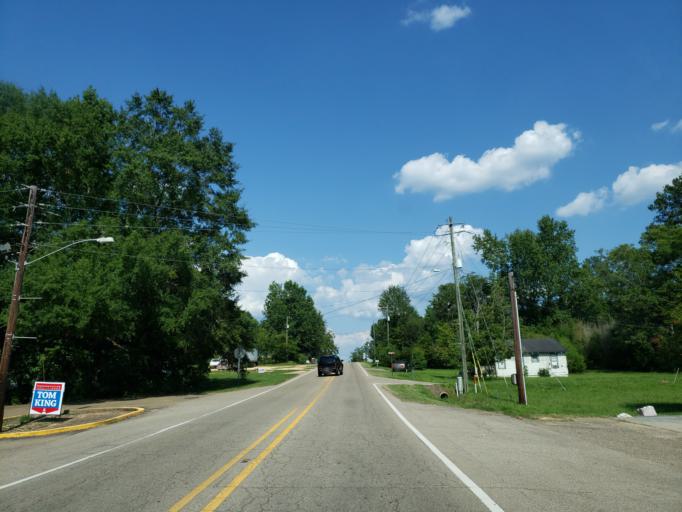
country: US
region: Mississippi
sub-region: Covington County
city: Collins
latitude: 31.5618
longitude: -89.4960
